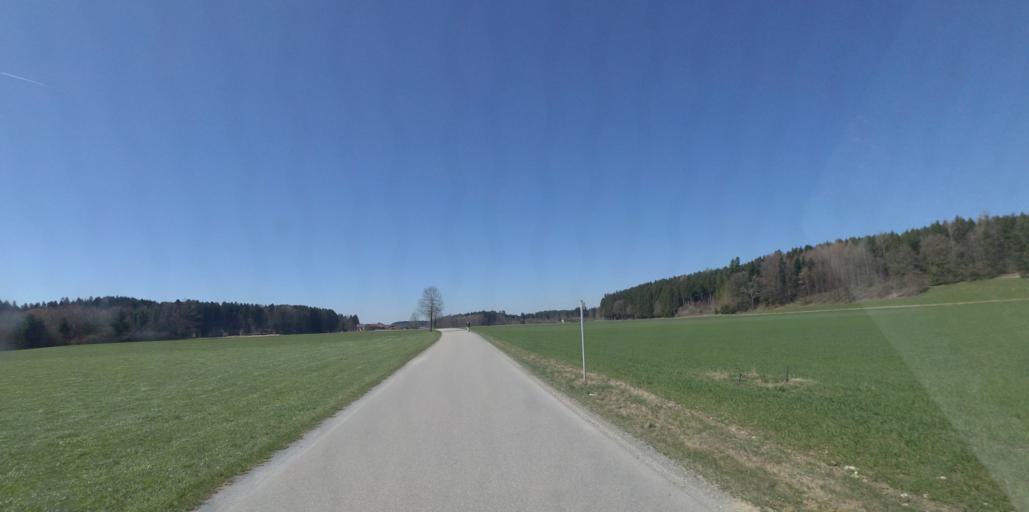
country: DE
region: Bavaria
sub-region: Upper Bavaria
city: Chieming
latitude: 47.9123
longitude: 12.5548
